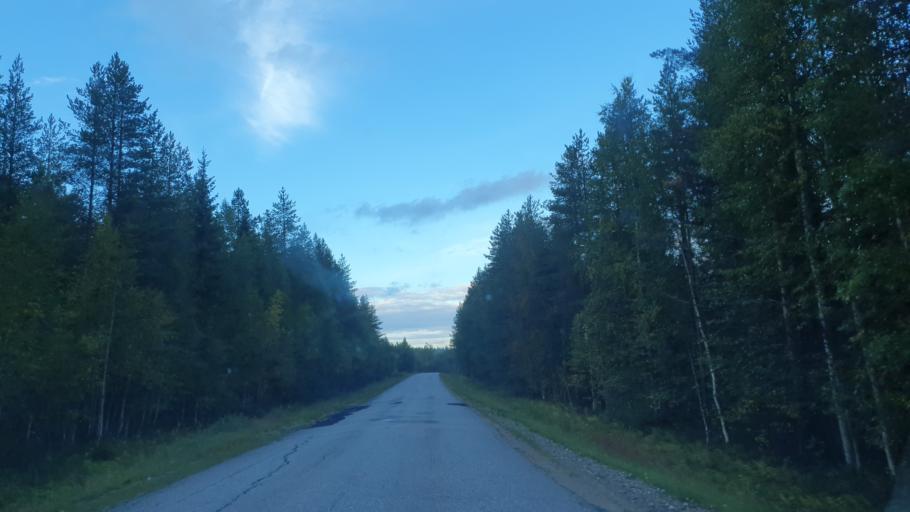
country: FI
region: Kainuu
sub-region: Kehys-Kainuu
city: Kuhmo
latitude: 64.4125
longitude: 29.8851
